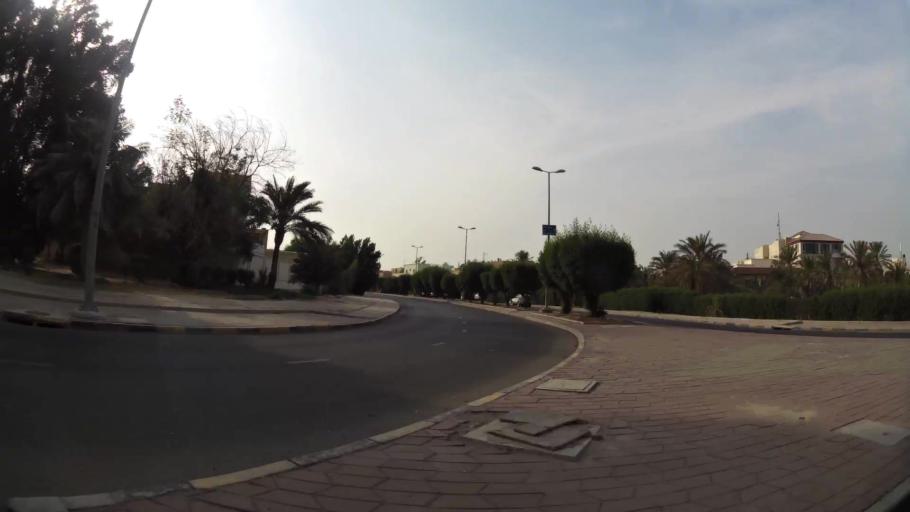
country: KW
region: Mubarak al Kabir
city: Sabah as Salim
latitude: 29.2609
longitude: 48.0561
